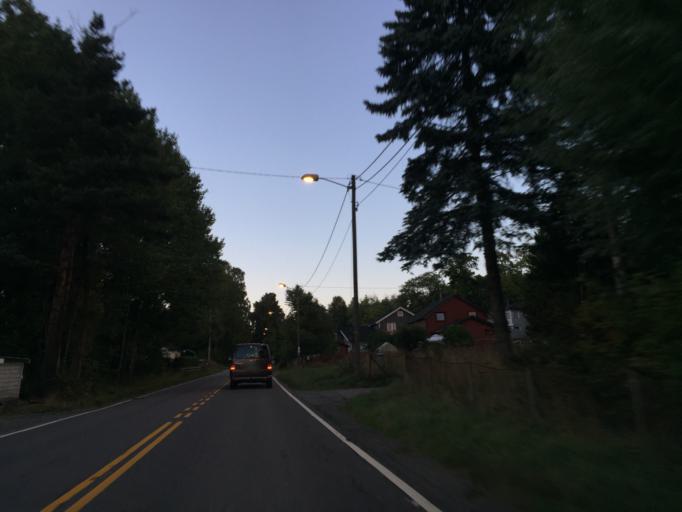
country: NO
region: Ostfold
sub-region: Moss
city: Moss
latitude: 59.4830
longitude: 10.6967
